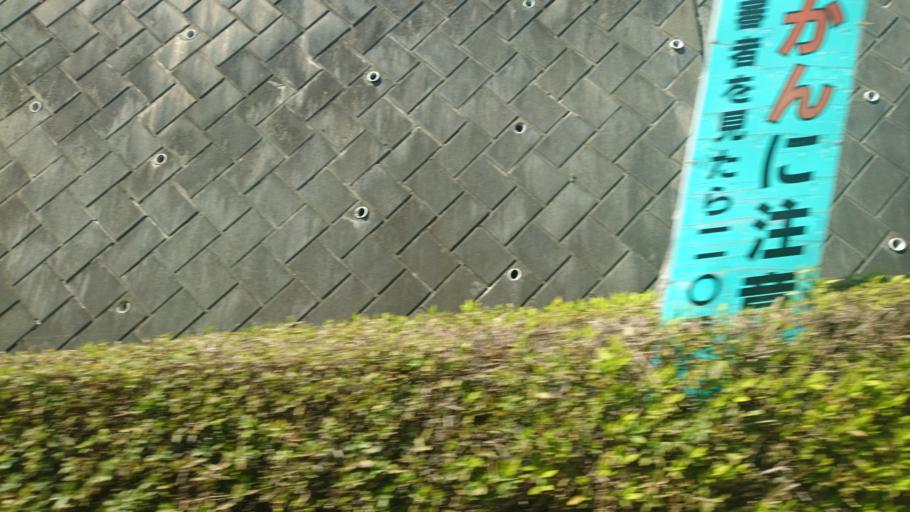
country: JP
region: Kanagawa
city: Fujisawa
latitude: 35.3739
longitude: 139.4314
